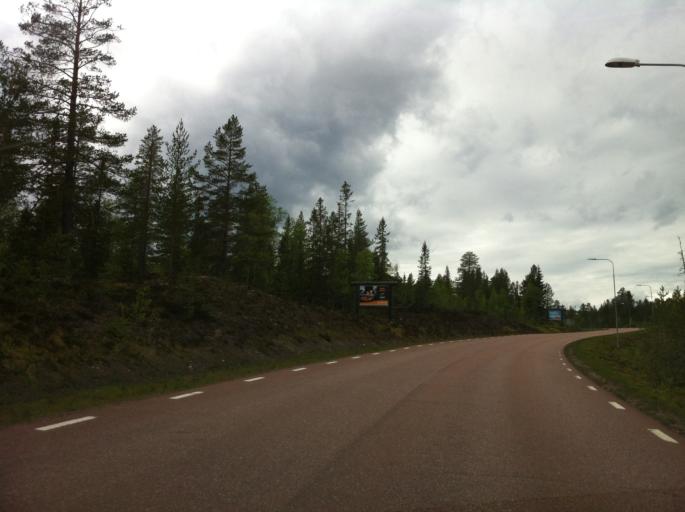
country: SE
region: Dalarna
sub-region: Malung-Saelens kommun
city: Malung
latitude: 61.1506
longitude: 13.2719
